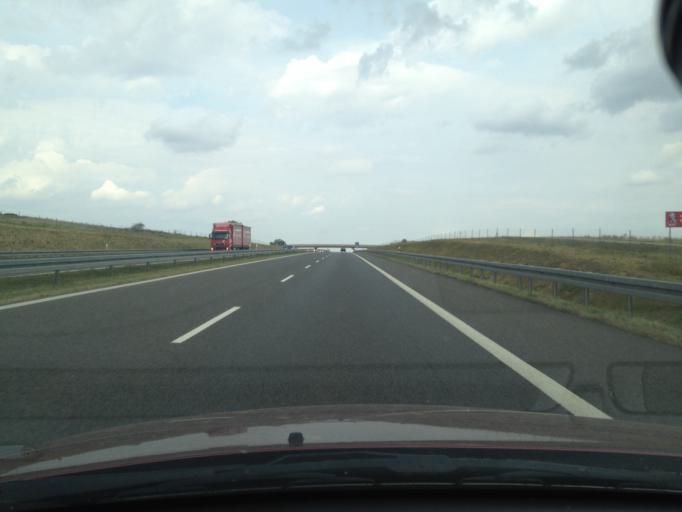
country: PL
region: West Pomeranian Voivodeship
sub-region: Powiat pyrzycki
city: Kozielice
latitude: 53.0265
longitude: 14.8629
